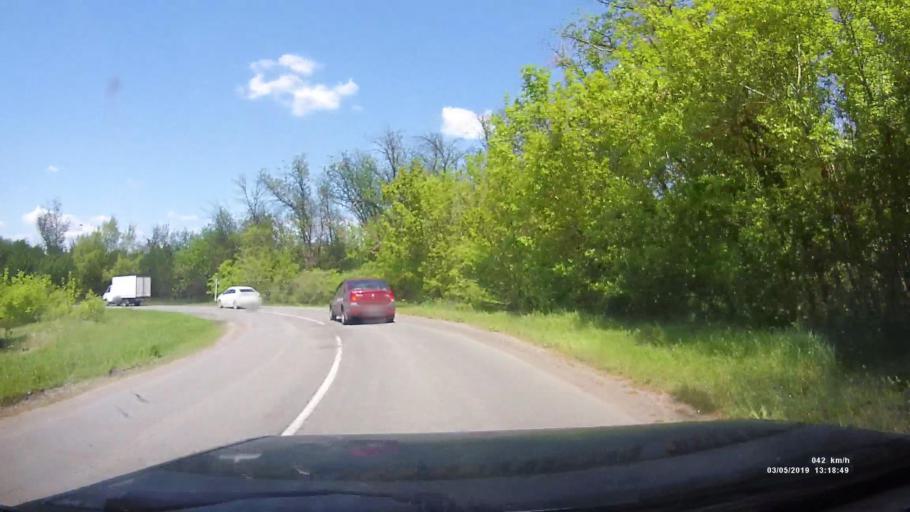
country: RU
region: Rostov
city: Semikarakorsk
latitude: 47.5346
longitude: 40.7511
